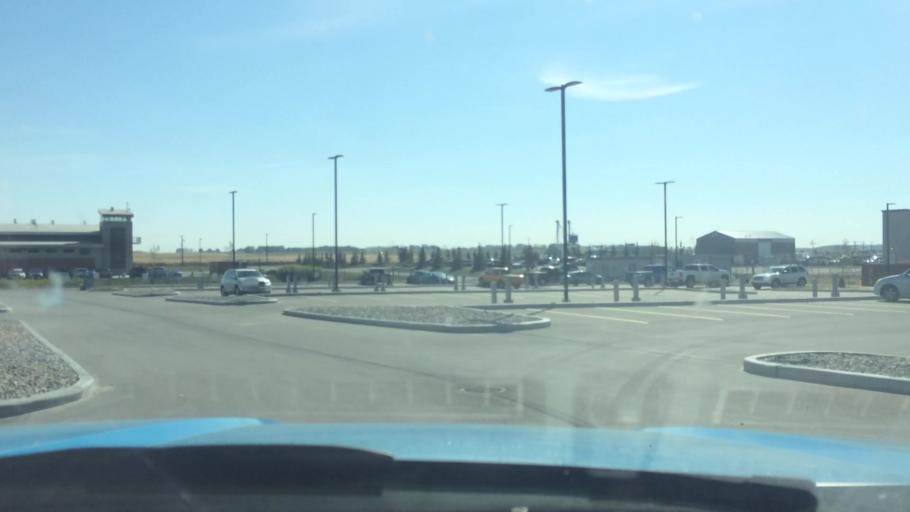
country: CA
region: Alberta
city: Airdrie
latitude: 51.2168
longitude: -113.9389
